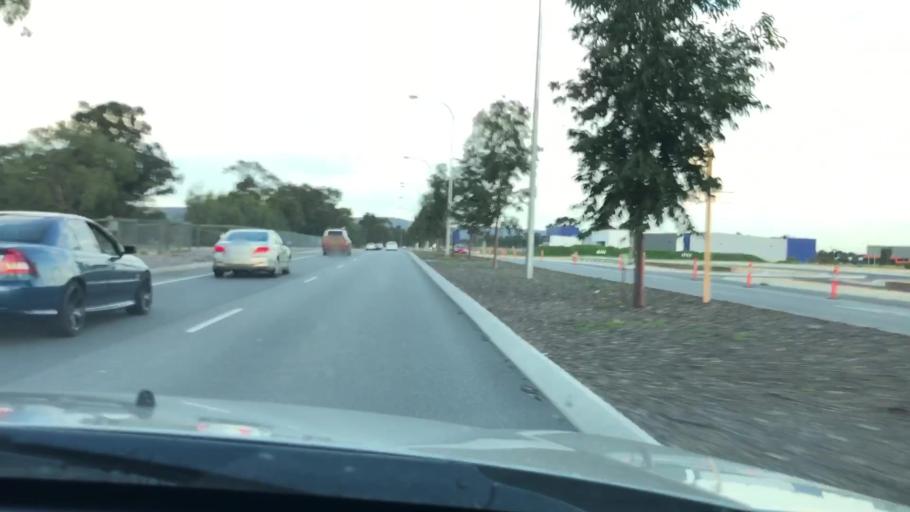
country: AU
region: Western Australia
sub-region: Armadale
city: Seville Grove
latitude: -32.1375
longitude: 115.9707
